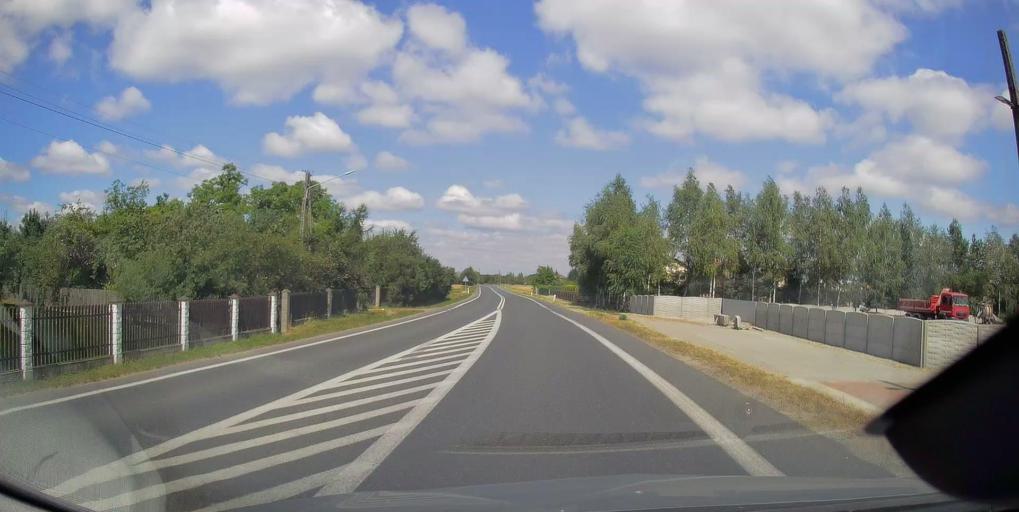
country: PL
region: Subcarpathian Voivodeship
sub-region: Powiat mielecki
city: Przeclaw
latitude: 50.1477
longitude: 21.4859
